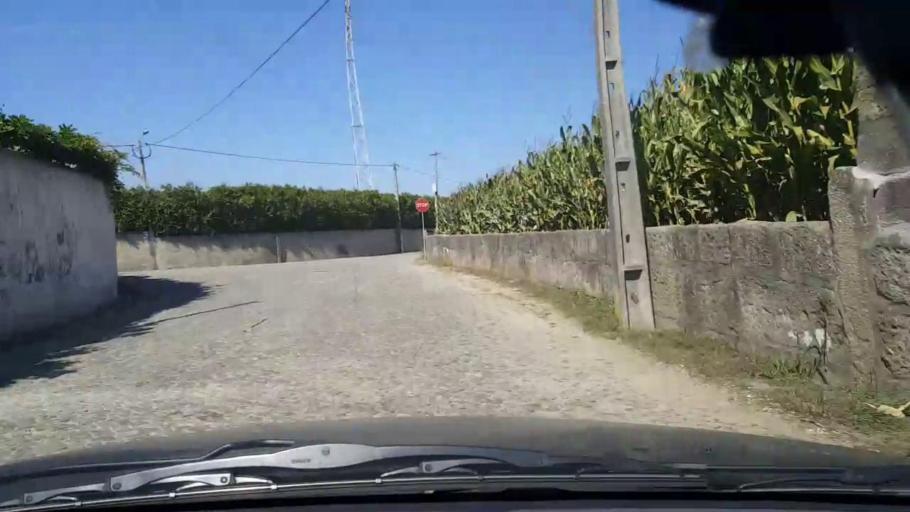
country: PT
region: Porto
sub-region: Matosinhos
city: Lavra
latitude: 41.2799
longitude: -8.7022
